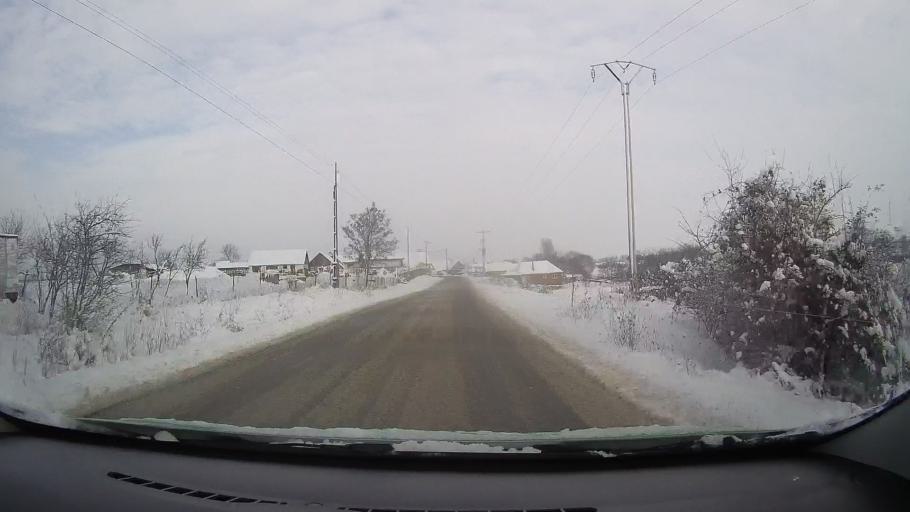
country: RO
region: Alba
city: Vurpar
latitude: 45.9719
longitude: 23.4806
